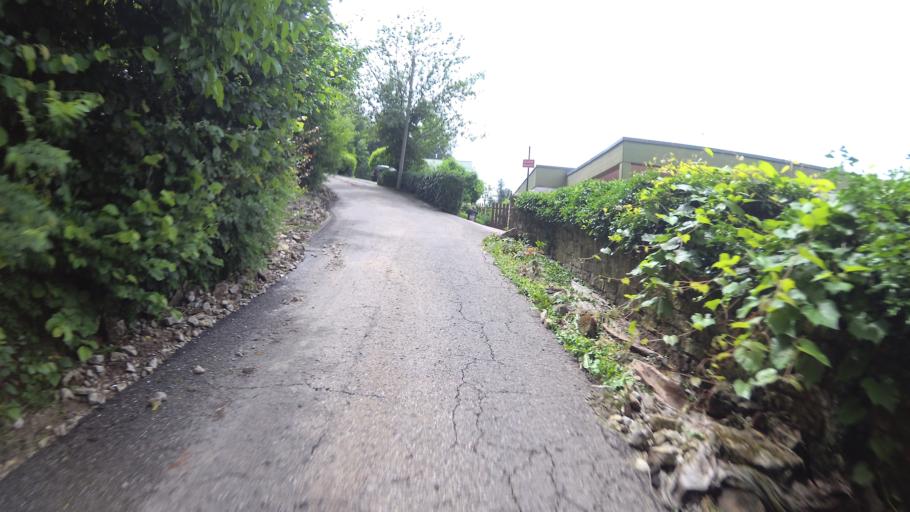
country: DE
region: Saarland
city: Kleinblittersdorf
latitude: 49.1528
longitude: 7.0445
